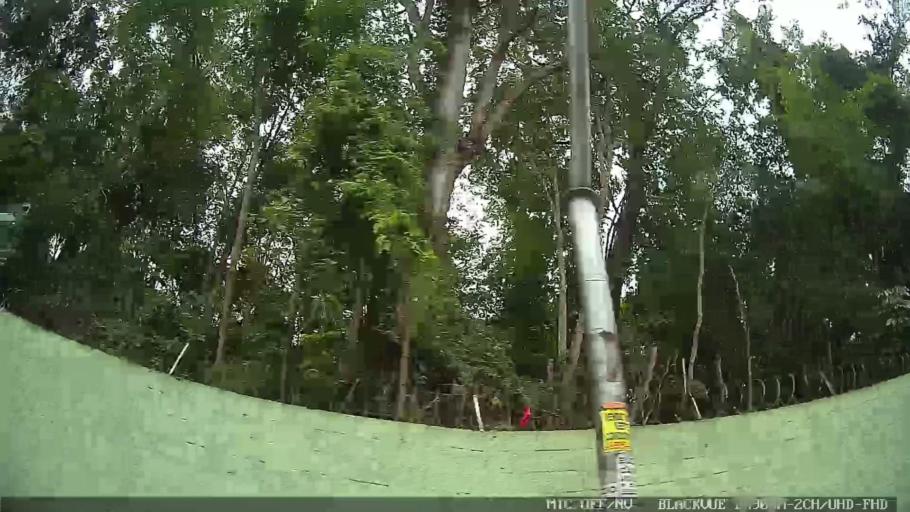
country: BR
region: Sao Paulo
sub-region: Osasco
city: Osasco
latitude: -23.5004
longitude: -46.7523
